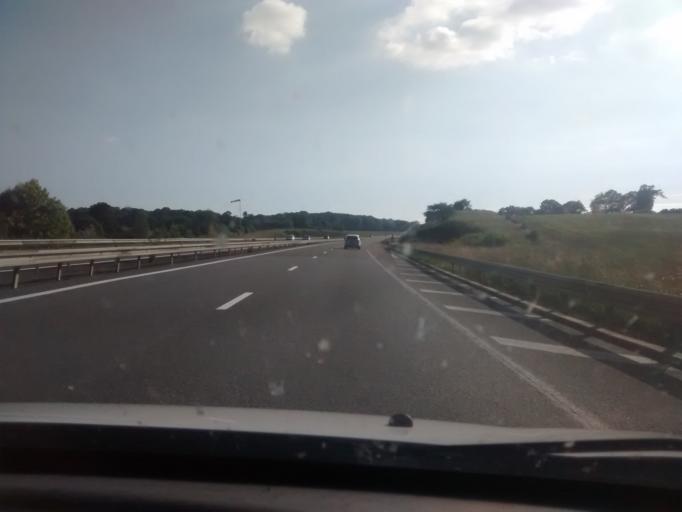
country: FR
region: Pays de la Loire
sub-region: Departement de la Mayenne
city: Saint-Berthevin
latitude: 48.0918
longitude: -0.8615
